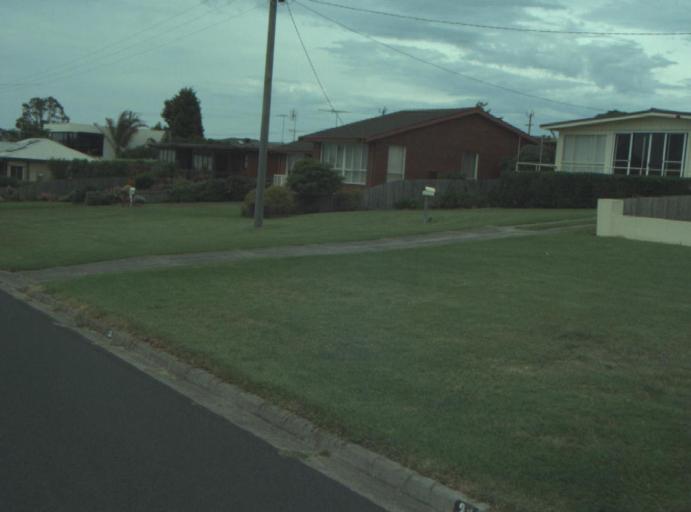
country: AU
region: Victoria
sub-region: Greater Geelong
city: Clifton Springs
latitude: -38.1128
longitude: 144.6636
